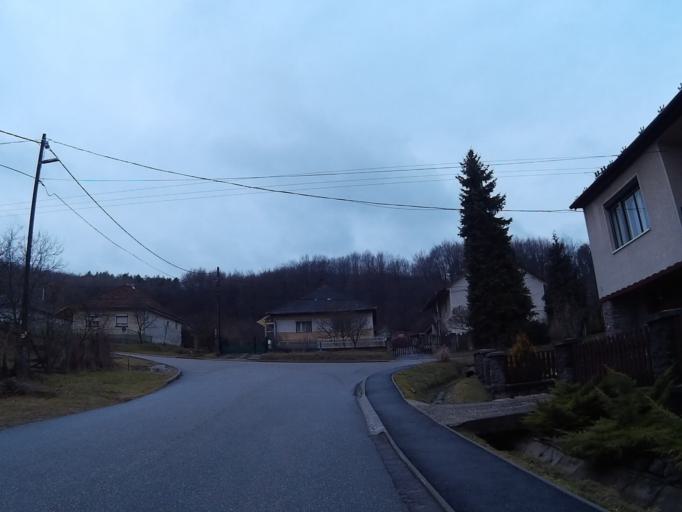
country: HU
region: Borsod-Abauj-Zemplen
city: Gonc
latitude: 48.5410
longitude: 21.4120
